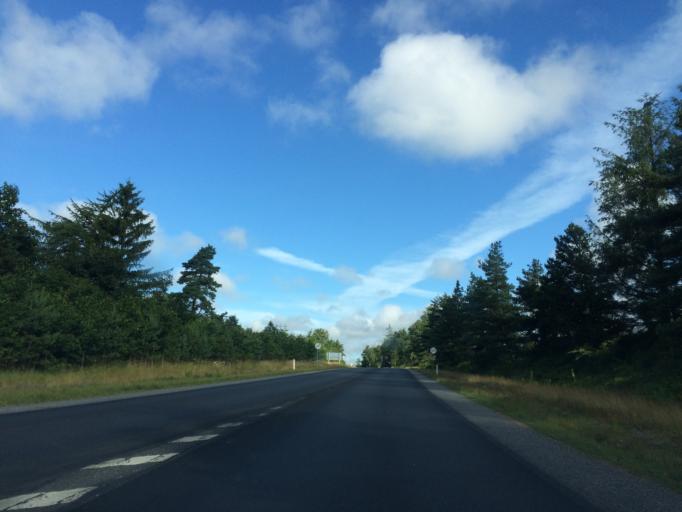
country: DK
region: Central Jutland
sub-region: Viborg Kommune
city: Bjerringbro
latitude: 56.2988
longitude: 9.6687
